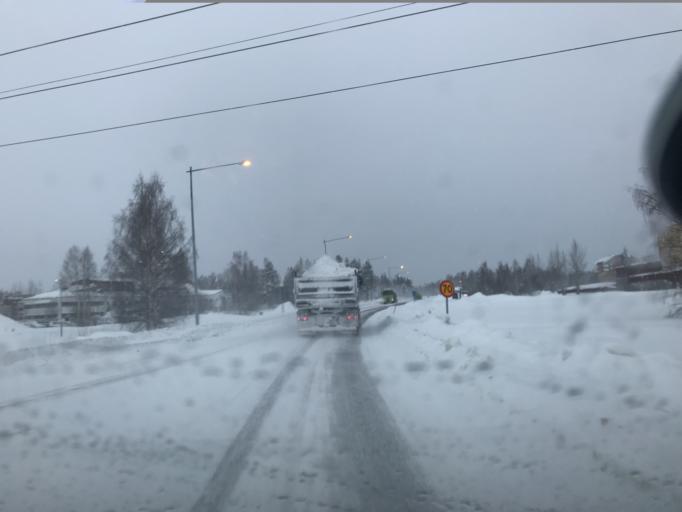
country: SE
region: Norrbotten
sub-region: Lulea Kommun
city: Lulea
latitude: 65.6155
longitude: 22.1323
